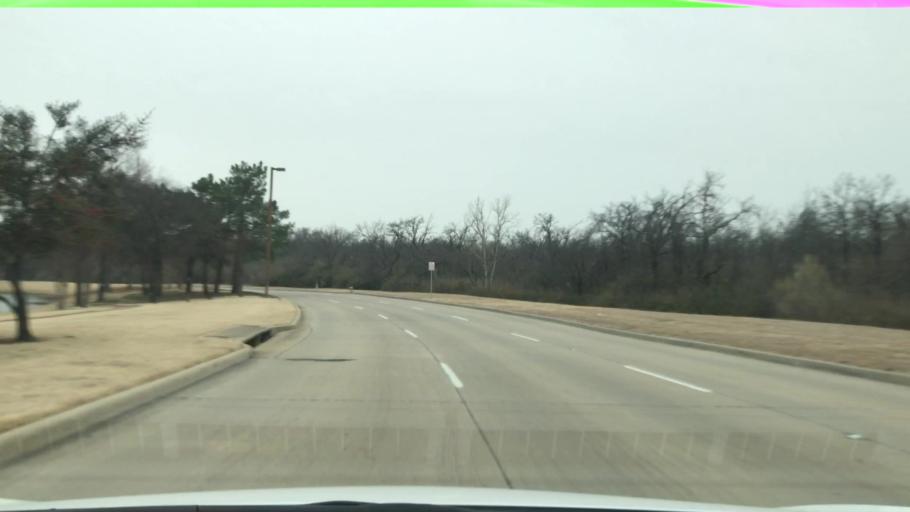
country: US
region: Texas
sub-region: Dallas County
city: Farmers Branch
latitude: 32.8948
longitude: -96.9520
